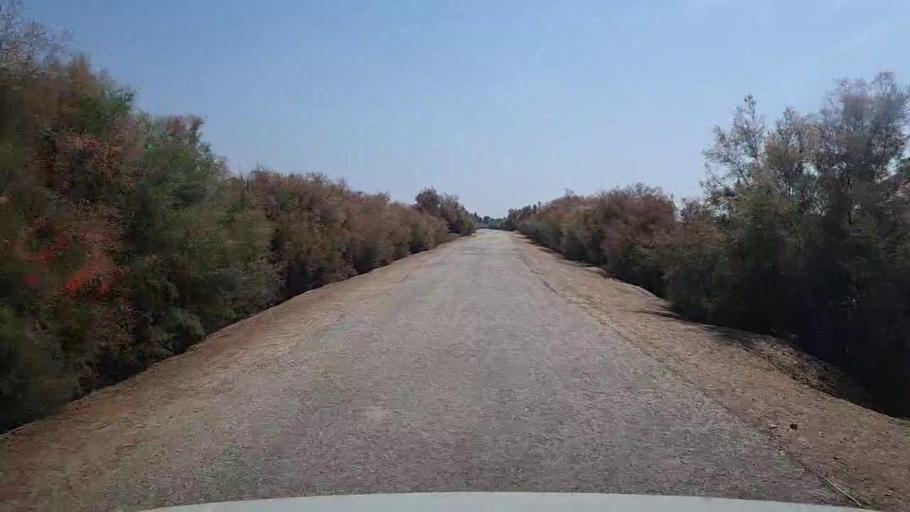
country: PK
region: Sindh
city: Kandhkot
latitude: 28.2989
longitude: 69.3522
